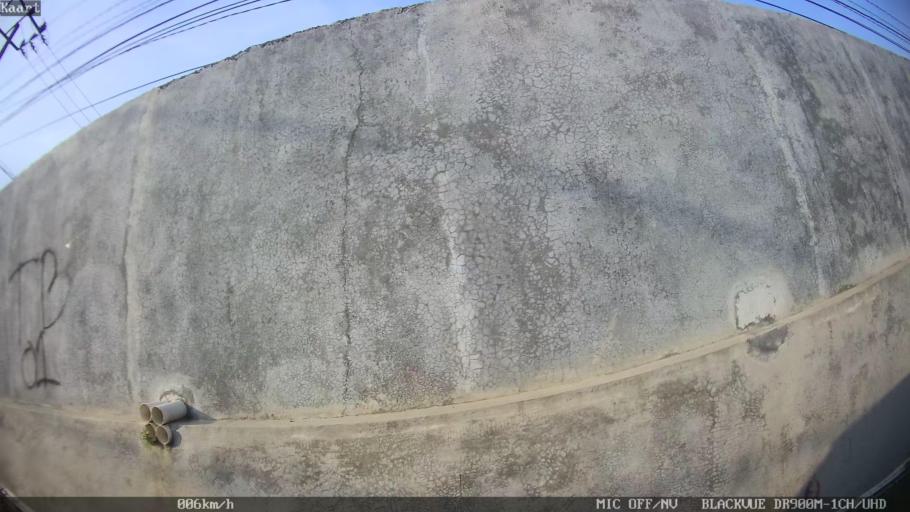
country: ID
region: Lampung
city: Kedaton
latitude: -5.3973
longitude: 105.2994
